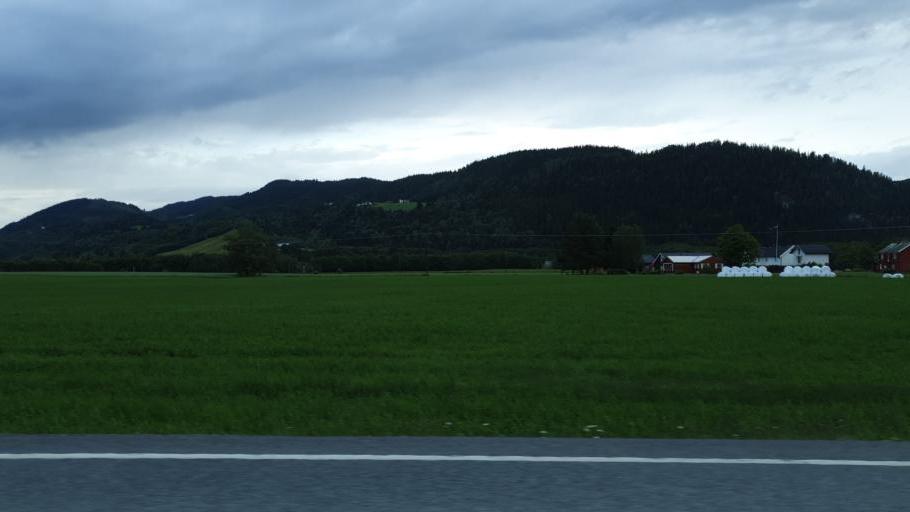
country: NO
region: Sor-Trondelag
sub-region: Melhus
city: Lundamo
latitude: 63.1833
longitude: 10.3150
